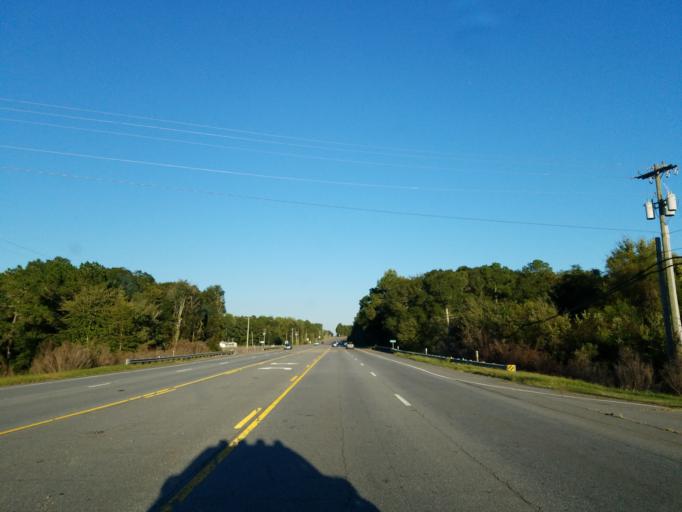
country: US
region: Georgia
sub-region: Worth County
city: Sylvester
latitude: 31.5274
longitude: -83.8055
